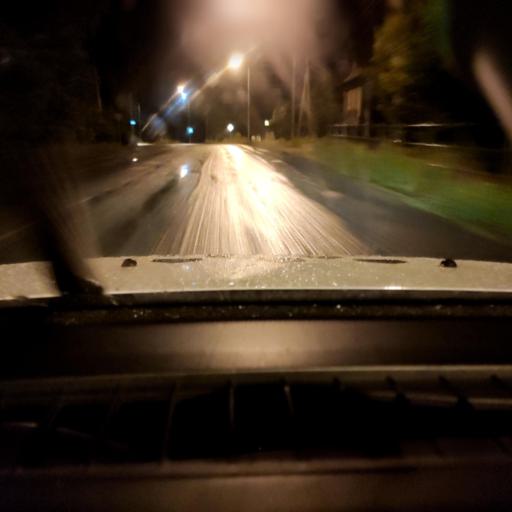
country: RU
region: Udmurtiya
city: Khokhryaki
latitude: 57.1884
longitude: 53.1545
